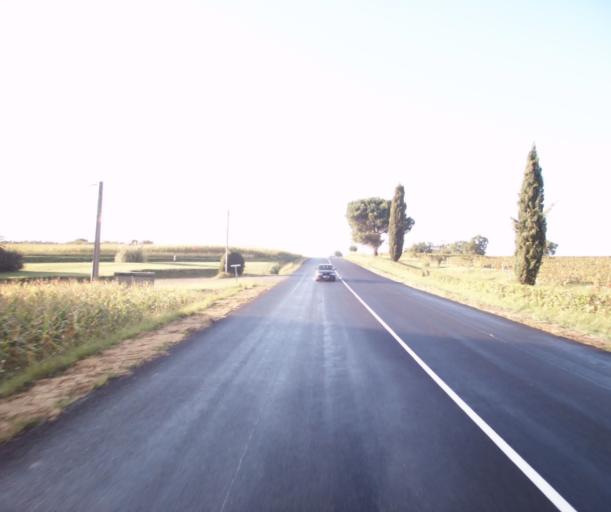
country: FR
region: Midi-Pyrenees
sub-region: Departement du Gers
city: Cazaubon
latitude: 43.9140
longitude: -0.0258
